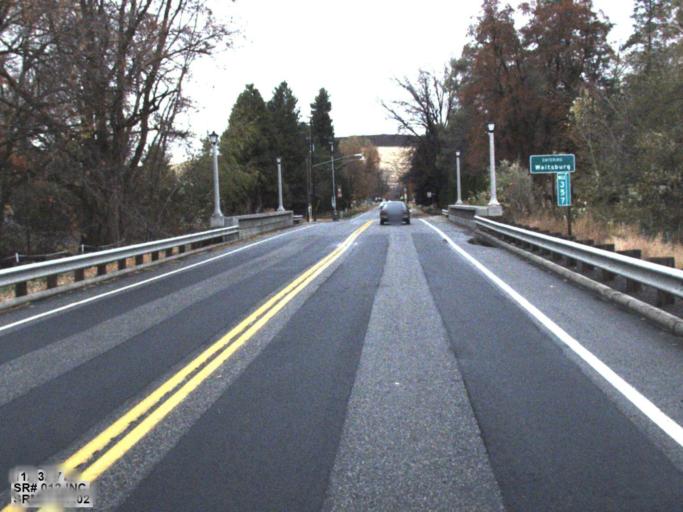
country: US
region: Washington
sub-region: Walla Walla County
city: Waitsburg
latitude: 46.2619
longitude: -118.1532
